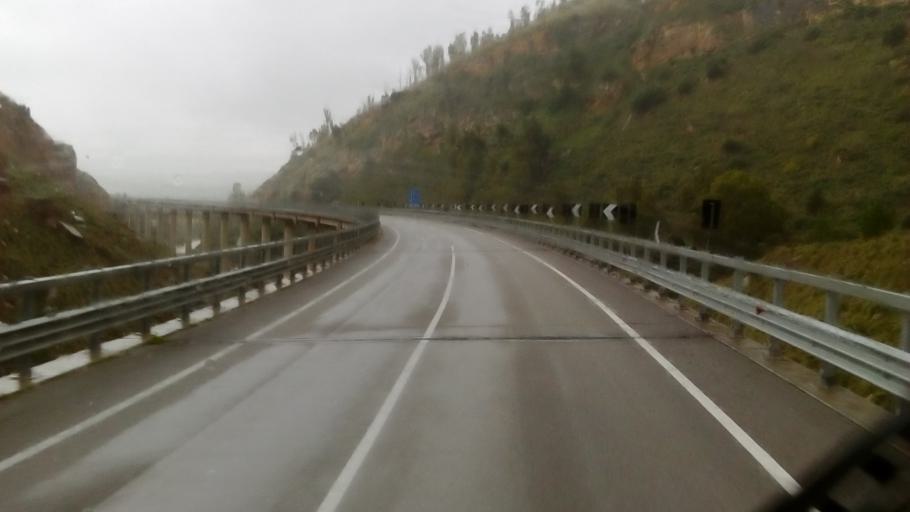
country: IT
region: Sicily
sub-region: Enna
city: Pietraperzia
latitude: 37.5005
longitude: 14.1410
